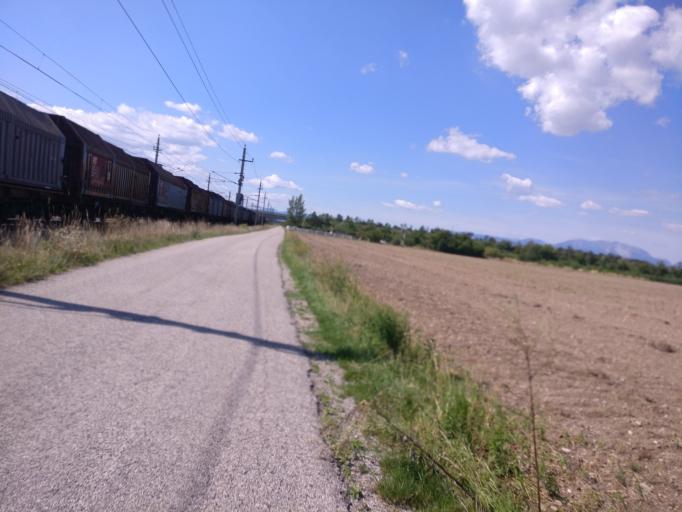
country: AT
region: Lower Austria
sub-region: Wiener Neustadt Stadt
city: Wiener Neustadt
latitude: 47.7926
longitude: 16.2095
